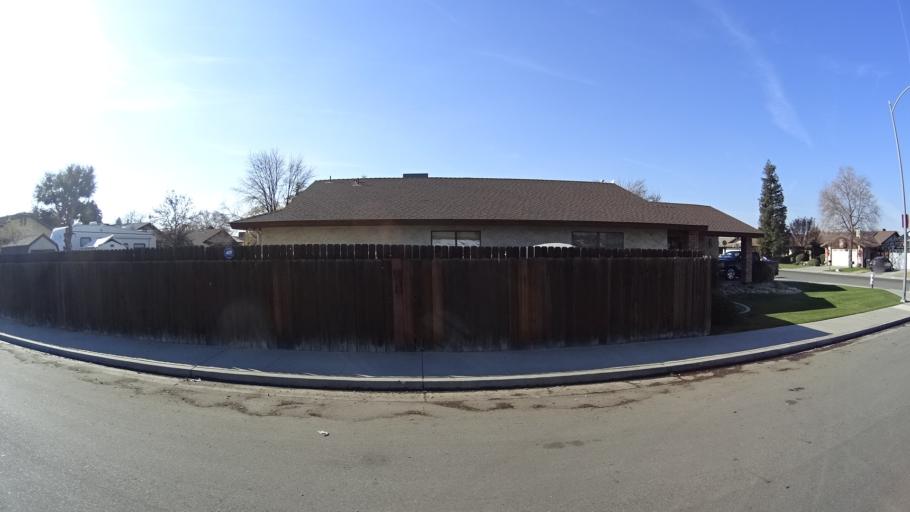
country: US
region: California
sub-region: Kern County
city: Greenfield
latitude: 35.3086
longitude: -119.0479
